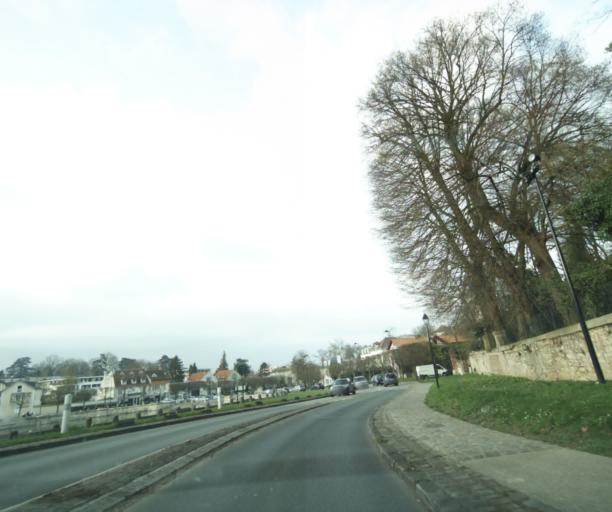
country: FR
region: Ile-de-France
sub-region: Departement des Yvelines
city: Louveciennes
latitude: 48.8662
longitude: 2.1020
